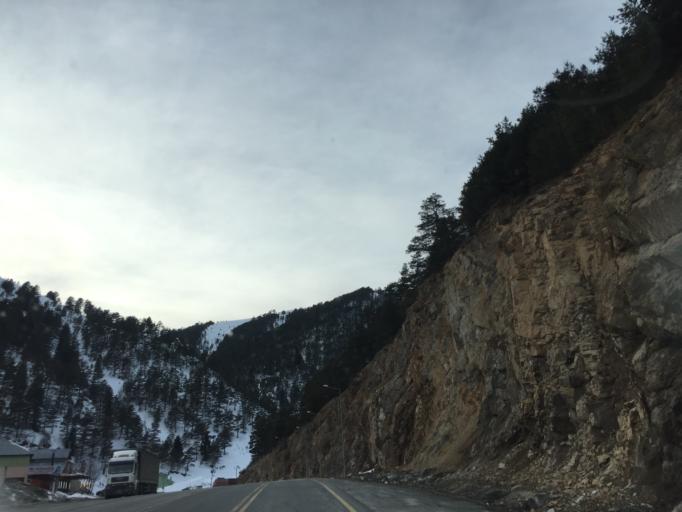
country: TR
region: Gumushane
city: Torul
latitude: 40.6560
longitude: 39.4031
